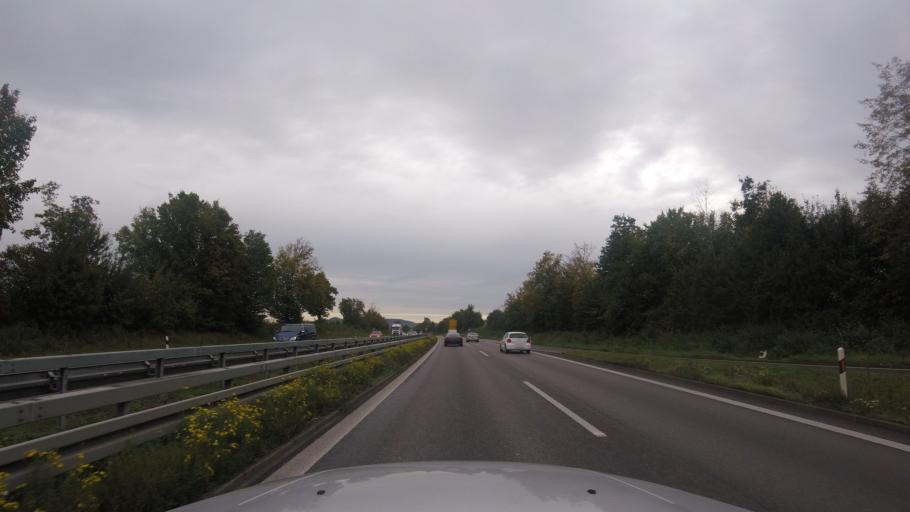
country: DE
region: Baden-Wuerttemberg
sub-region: Regierungsbezirk Stuttgart
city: Weinstadt-Endersbach
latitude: 48.8159
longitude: 9.3378
